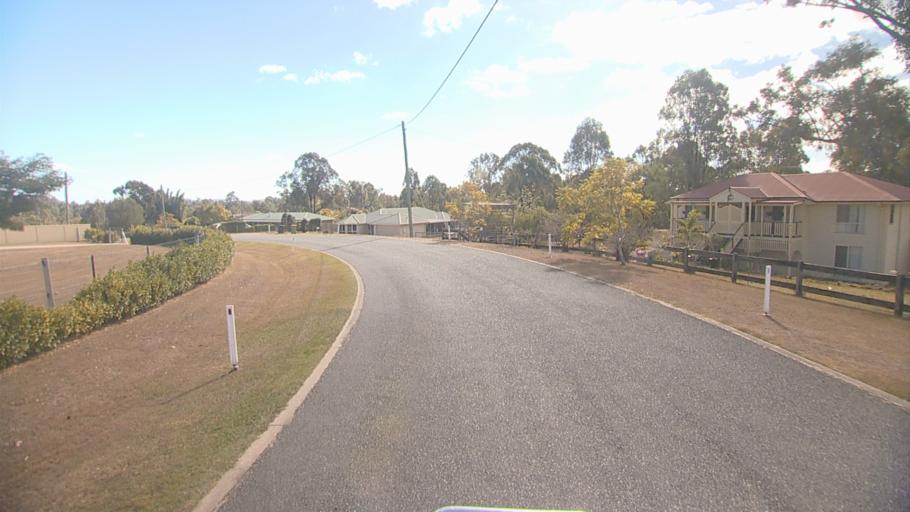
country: AU
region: Queensland
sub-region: Logan
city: Cedar Vale
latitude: -27.8763
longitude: 153.0043
